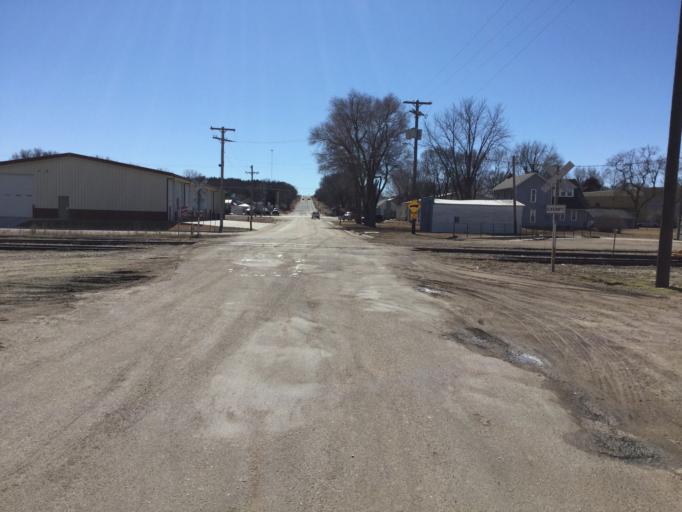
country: US
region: Kansas
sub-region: Marshall County
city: Blue Rapids
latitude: 39.6914
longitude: -96.7511
